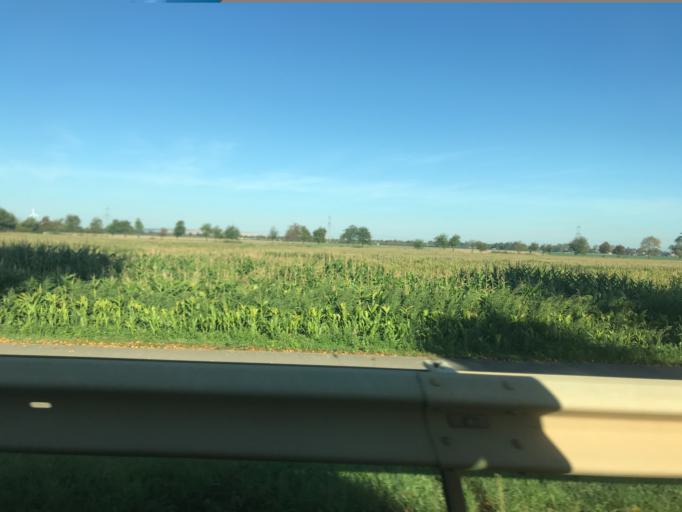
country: DE
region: North Rhine-Westphalia
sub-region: Regierungsbezirk Koln
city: Merzenich
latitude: 50.8401
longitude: 6.5927
